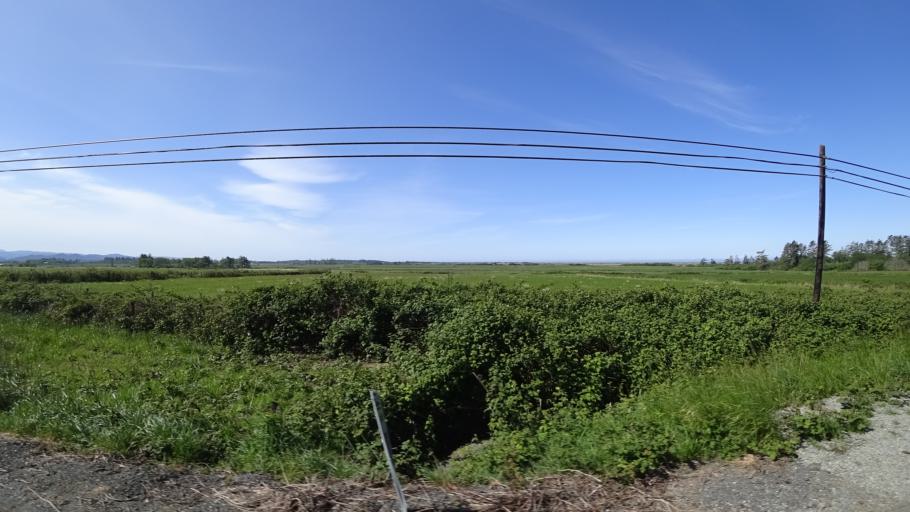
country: US
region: Oregon
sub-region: Curry County
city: Harbor
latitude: 41.9410
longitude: -124.1847
